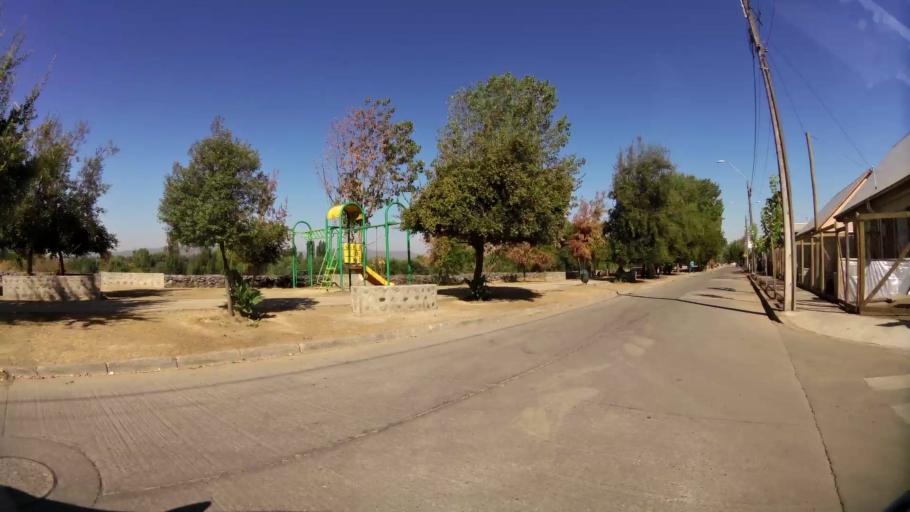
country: CL
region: Maule
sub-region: Provincia de Curico
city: Curico
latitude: -34.9965
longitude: -71.2614
